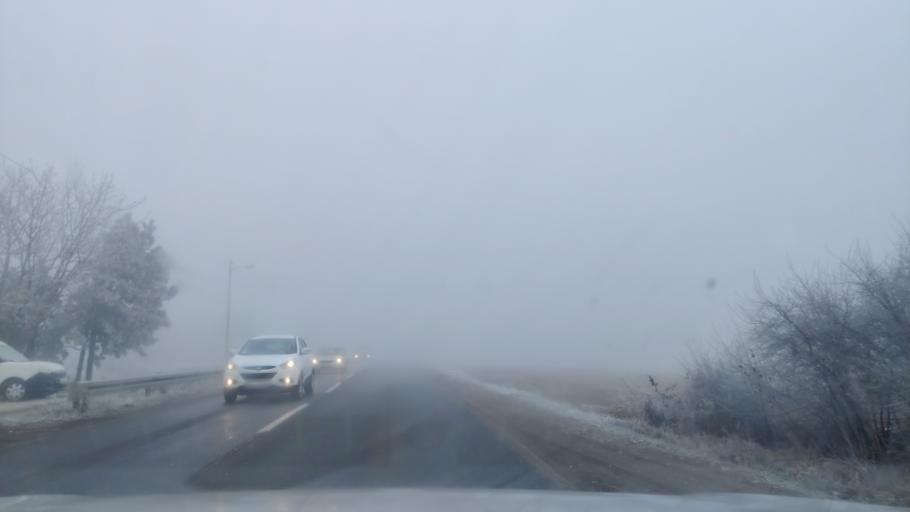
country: RS
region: Central Serbia
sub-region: Belgrade
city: Zemun
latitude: 44.8958
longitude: 20.4553
